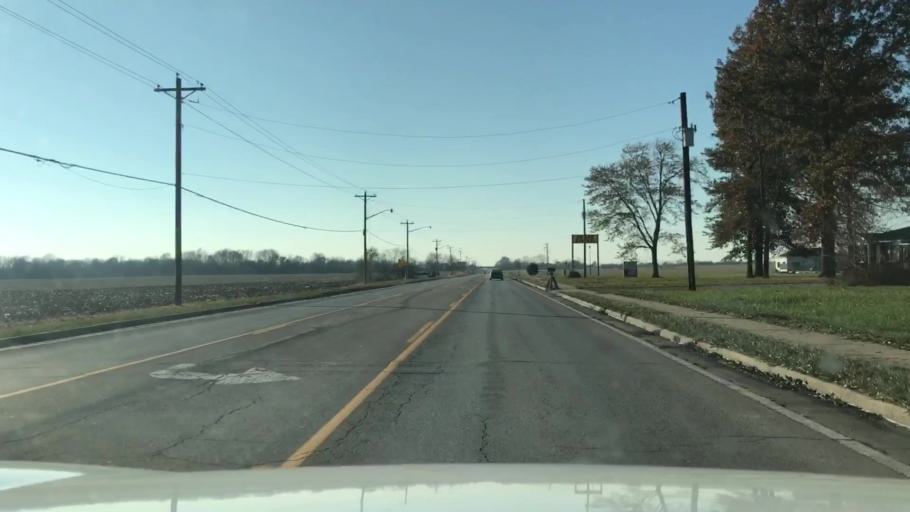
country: US
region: Illinois
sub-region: Clinton County
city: New Baden
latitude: 38.5352
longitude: -89.7119
